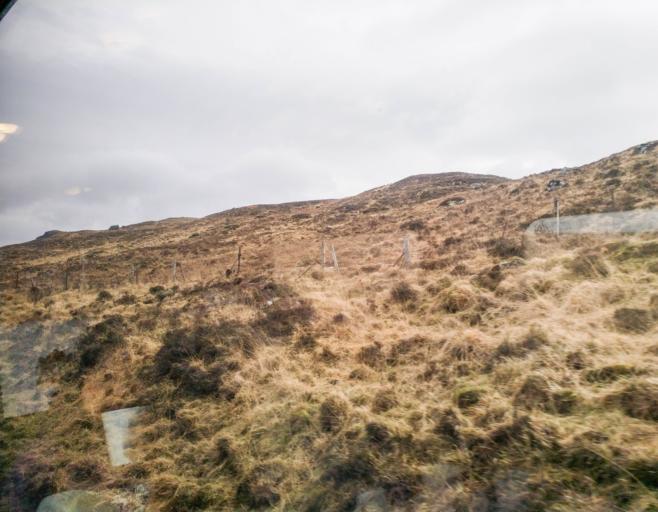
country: GB
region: Scotland
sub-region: Highland
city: Spean Bridge
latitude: 56.5883
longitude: -4.6566
